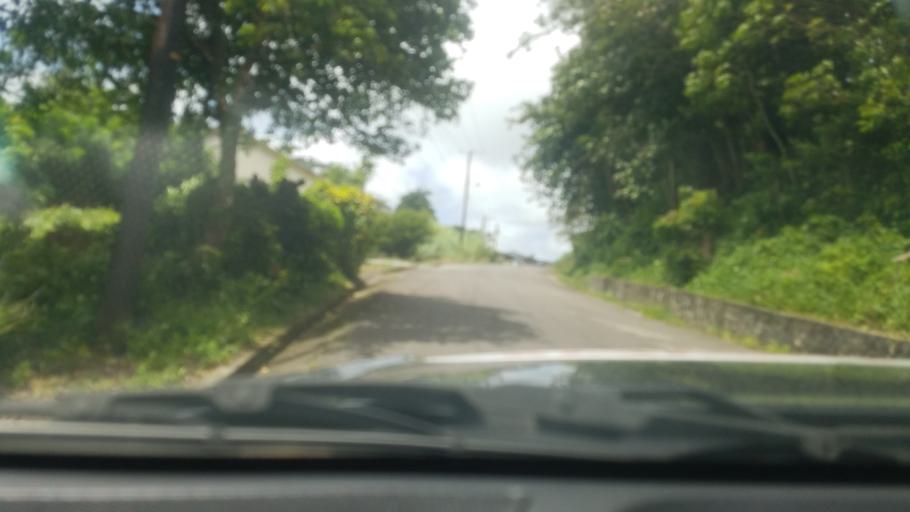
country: LC
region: Laborie Quarter
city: Laborie
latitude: 13.7932
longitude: -60.9549
